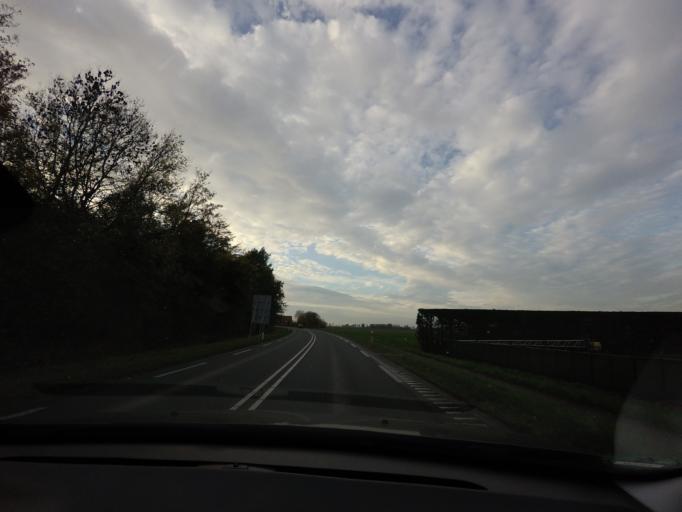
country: NL
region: Flevoland
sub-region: Gemeente Noordoostpolder
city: Ens
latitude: 52.7143
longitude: 5.8643
